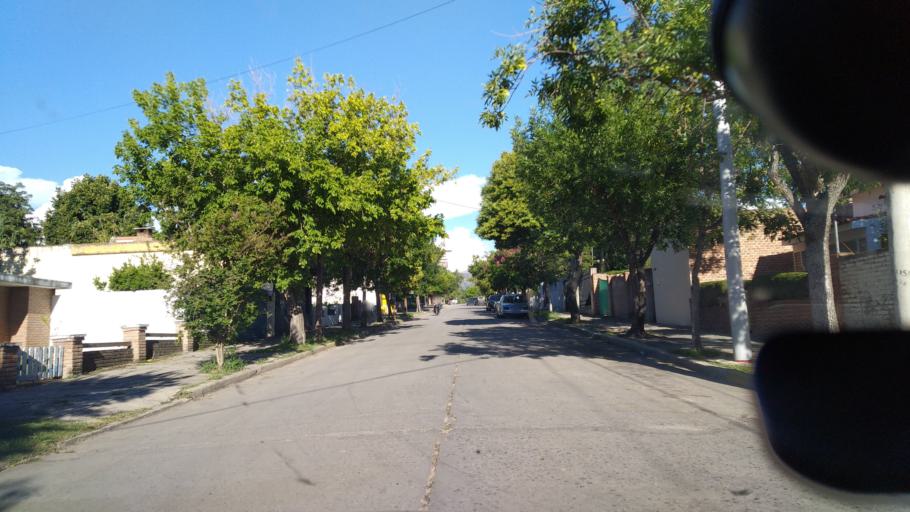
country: AR
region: Cordoba
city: Mina Clavero
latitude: -31.7282
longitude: -65.0029
